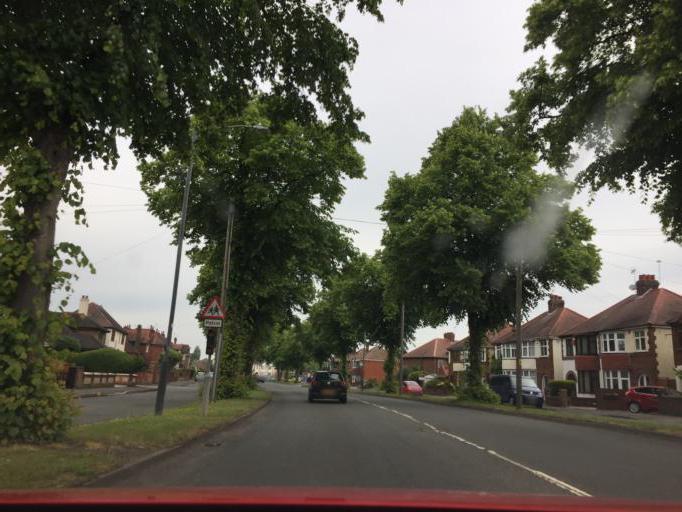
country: GB
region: England
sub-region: Warwickshire
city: Attleborough
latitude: 52.5149
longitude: -1.4551
